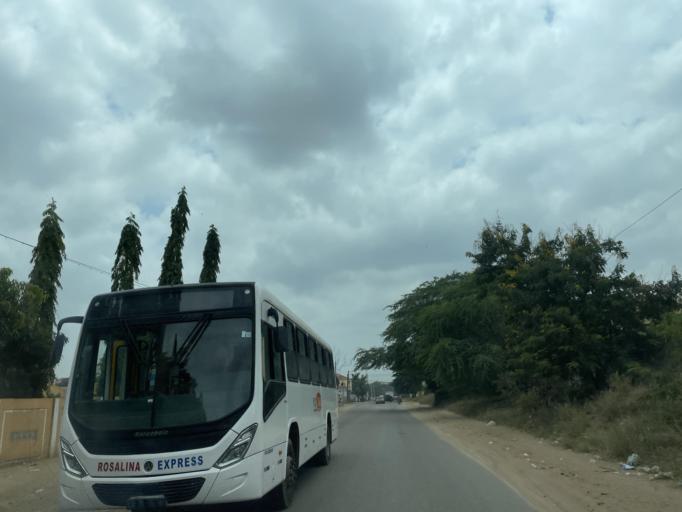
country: AO
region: Luanda
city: Luanda
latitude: -8.9132
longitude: 13.3763
